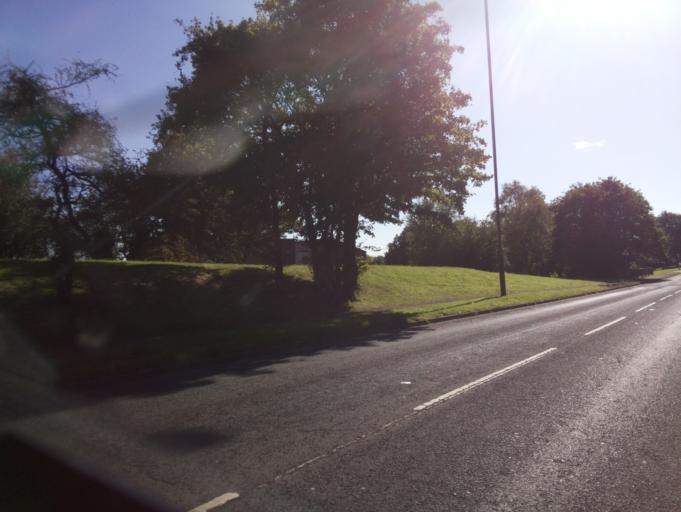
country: GB
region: Wales
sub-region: Torfaen County Borough
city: Cwmbran
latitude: 51.6533
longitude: -3.0476
